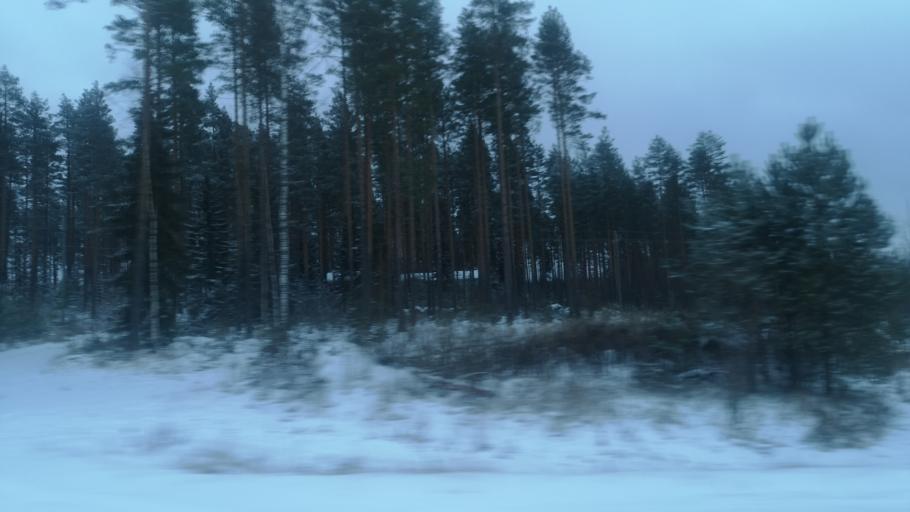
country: FI
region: Southern Savonia
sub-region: Savonlinna
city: Enonkoski
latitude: 62.0243
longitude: 28.7290
